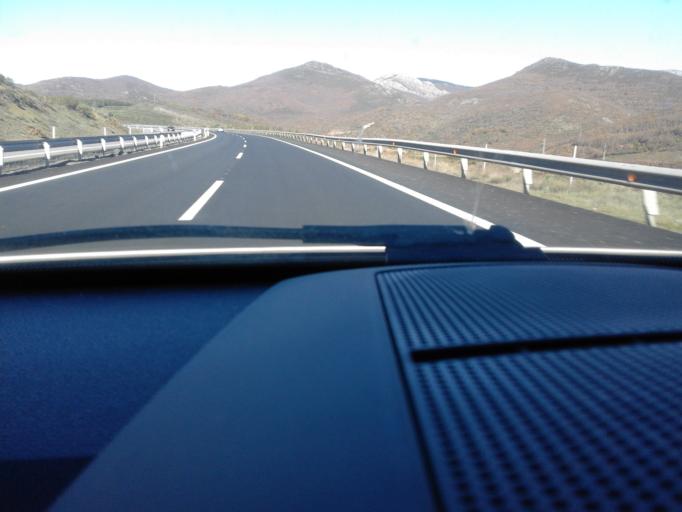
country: ES
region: Castille and Leon
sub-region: Provincia de Leon
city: Soto y Amio
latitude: 42.8063
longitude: -5.8334
